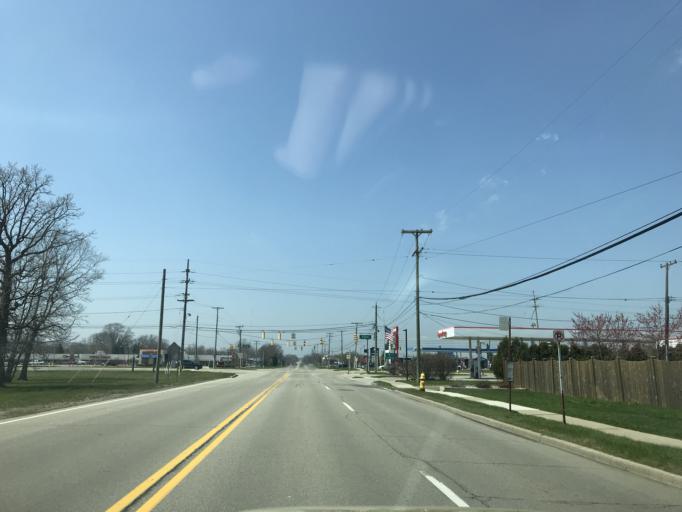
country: US
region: Michigan
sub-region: Wayne County
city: Riverview
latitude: 42.1704
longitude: -83.1875
